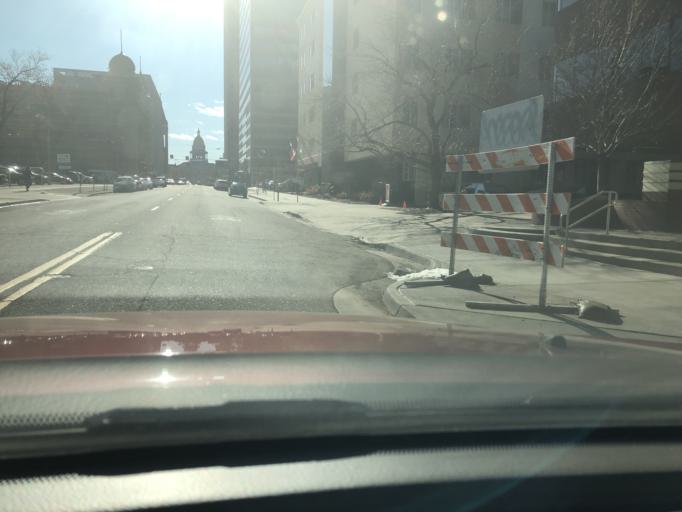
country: US
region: Colorado
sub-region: Denver County
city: Denver
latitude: 39.7462
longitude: -104.9849
